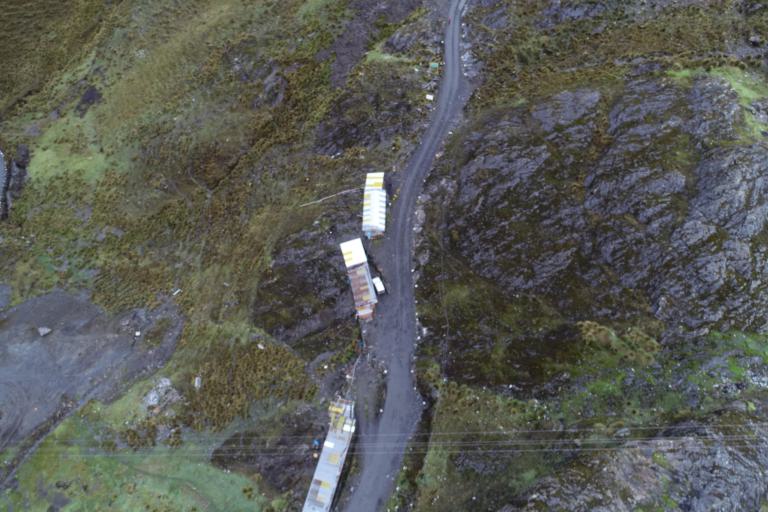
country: BO
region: La Paz
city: Sorata
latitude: -15.6630
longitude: -68.5113
